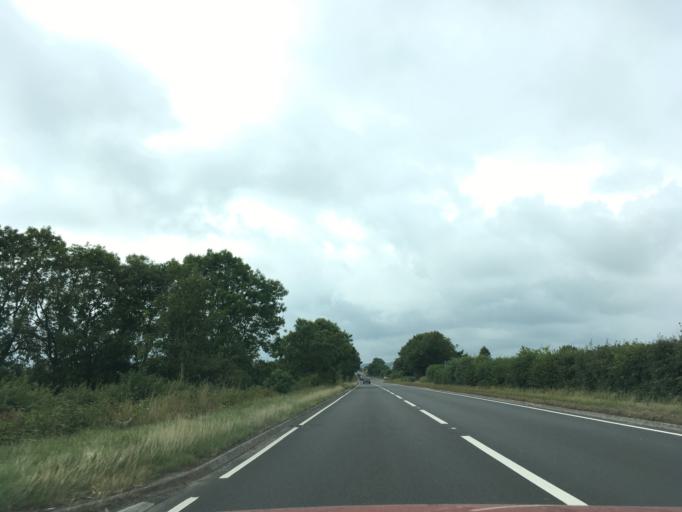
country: GB
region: Wales
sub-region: Carmarthenshire
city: Llanddowror
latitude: 51.8223
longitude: -4.5275
